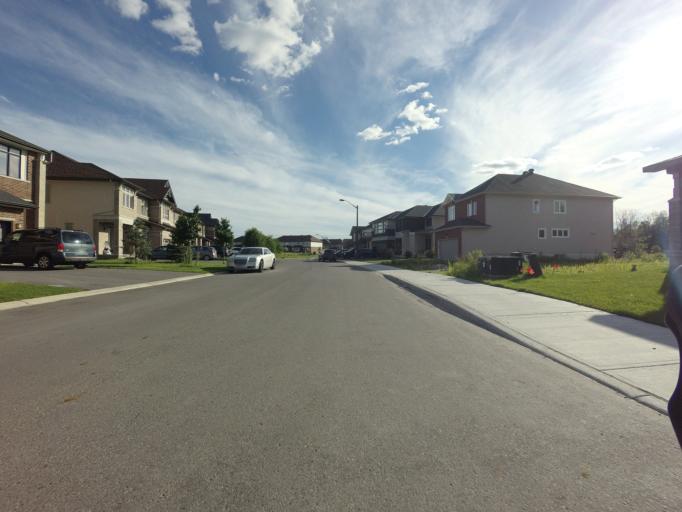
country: CA
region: Ontario
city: Ottawa
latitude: 45.2871
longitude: -75.6671
